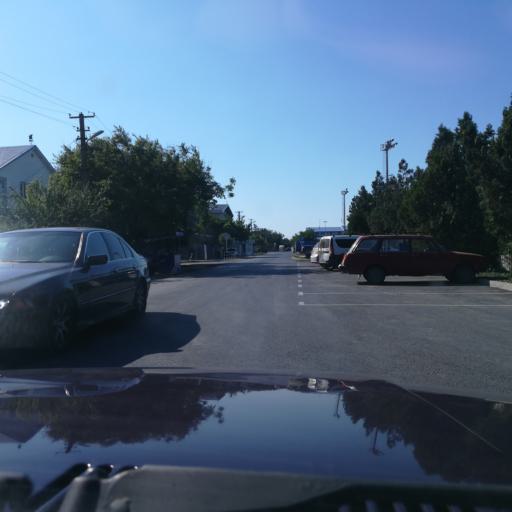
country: RU
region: Krasnodarskiy
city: Vityazevo
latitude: 45.0033
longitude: 37.2866
